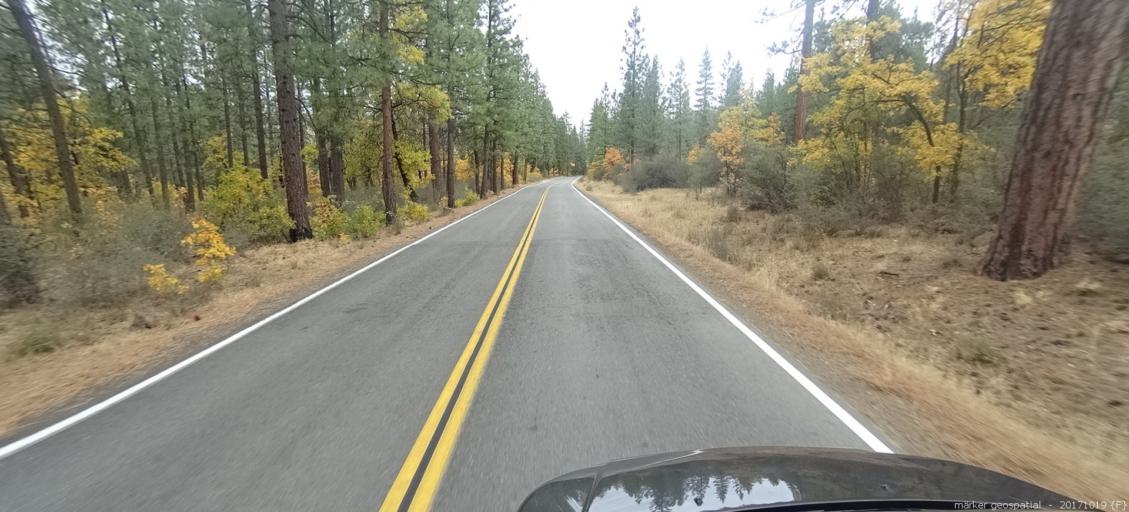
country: US
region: California
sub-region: Shasta County
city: Burney
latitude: 41.1776
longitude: -121.3622
